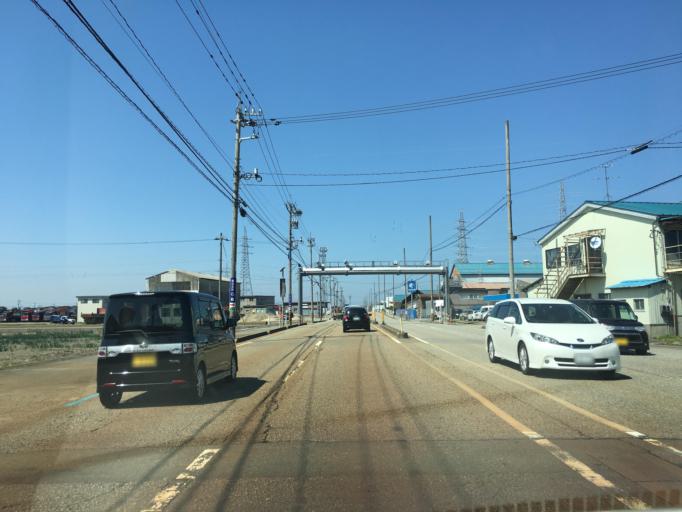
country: JP
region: Toyama
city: Toyama-shi
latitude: 36.7469
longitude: 137.2080
